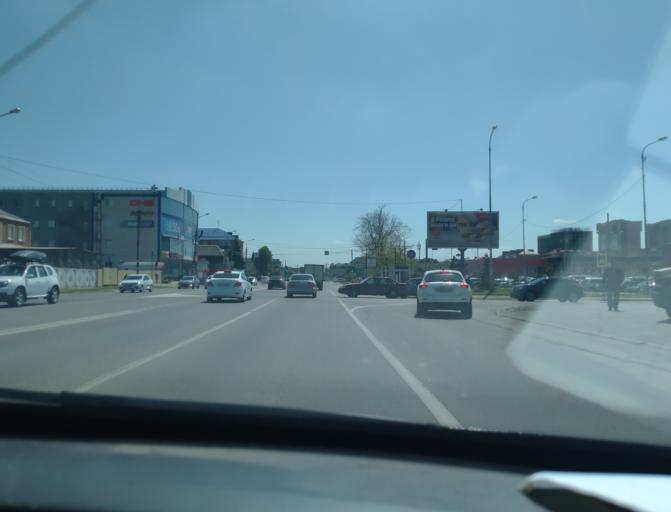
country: RU
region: Krasnodarskiy
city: Krasnodar
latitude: 45.0882
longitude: 39.0141
